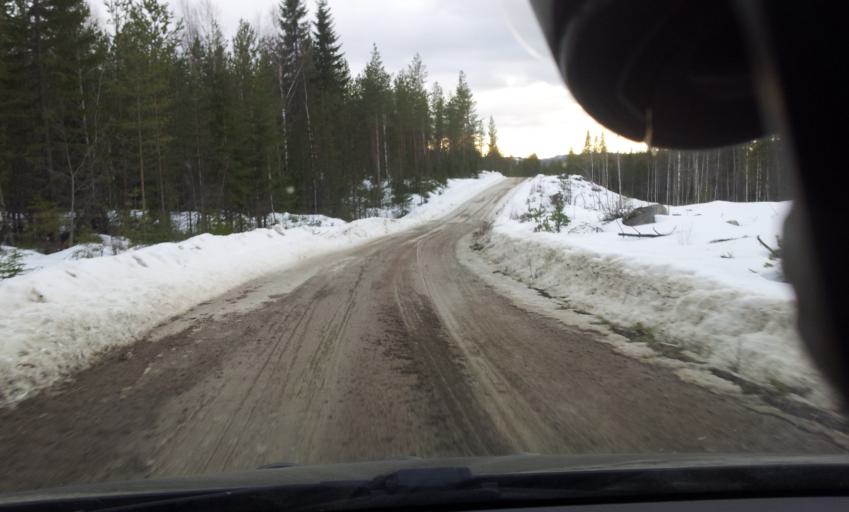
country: SE
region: Vaesternorrland
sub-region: Ange Kommun
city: Ange
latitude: 62.1908
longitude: 15.6861
